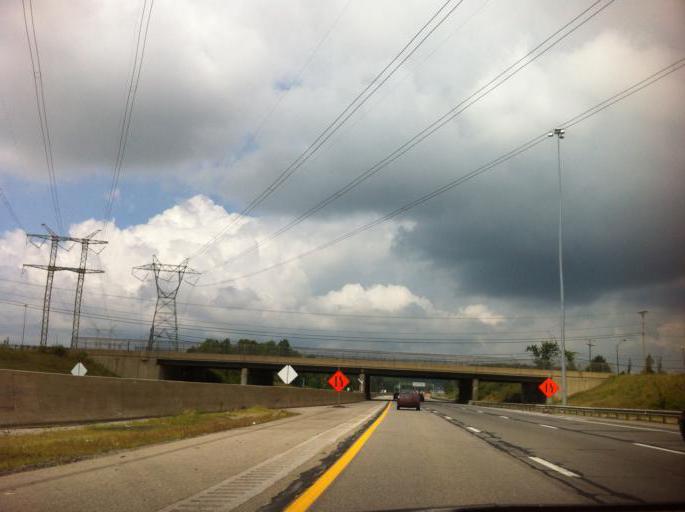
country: US
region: Ohio
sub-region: Summit County
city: Richfield
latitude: 41.2730
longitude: -81.6269
